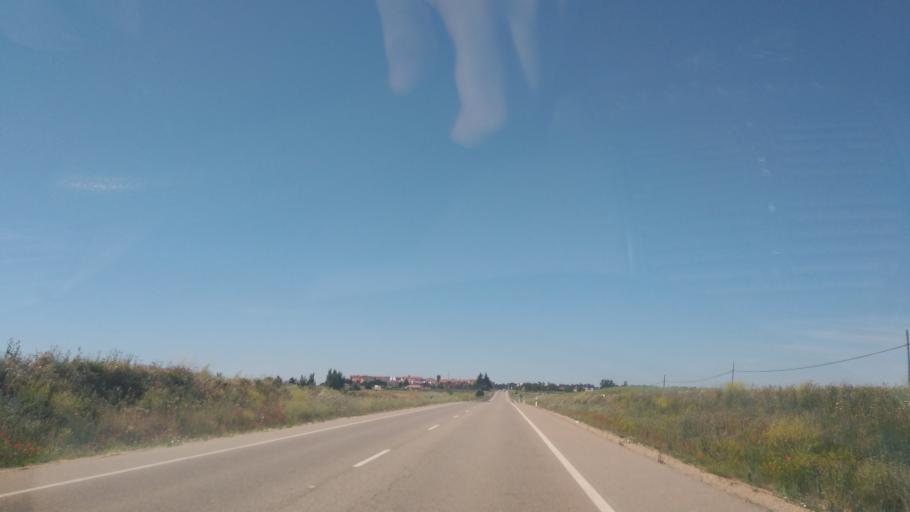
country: ES
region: Castille and Leon
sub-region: Provincia de Salamanca
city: Villares de la Reina
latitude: 41.0096
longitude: -5.6686
